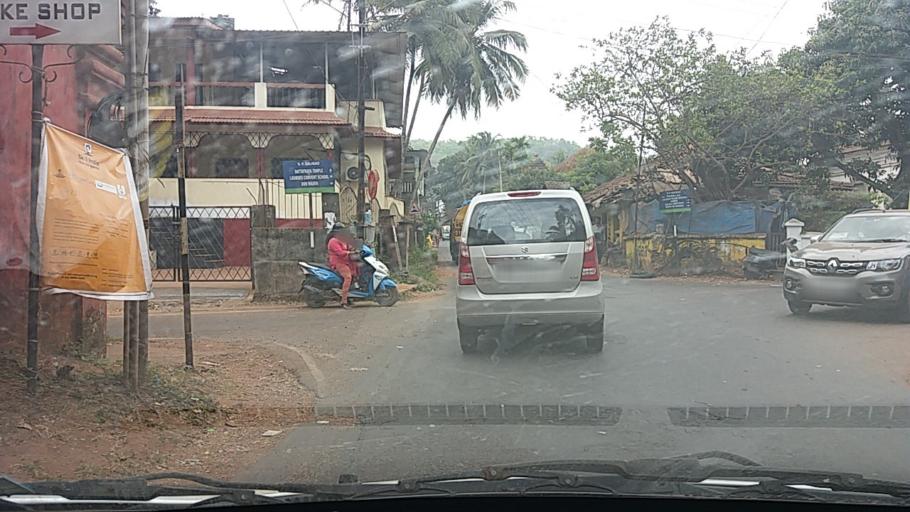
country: IN
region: Goa
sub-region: North Goa
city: Saligao
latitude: 15.5409
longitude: 73.7896
